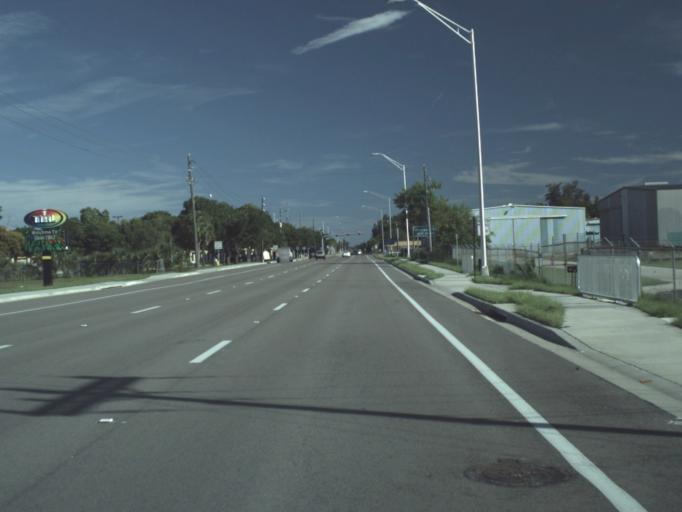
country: US
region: Florida
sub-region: Lee County
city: Fort Myers
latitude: 26.6199
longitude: -81.8599
